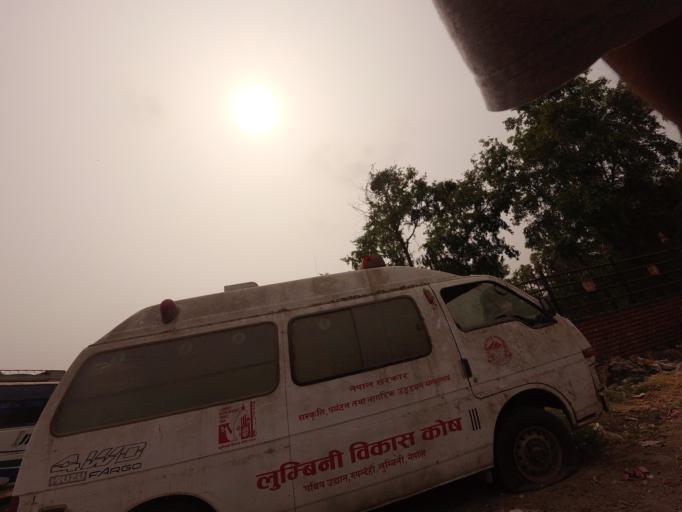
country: IN
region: Uttar Pradesh
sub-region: Maharajganj
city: Nautanwa
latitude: 27.4913
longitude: 83.2681
